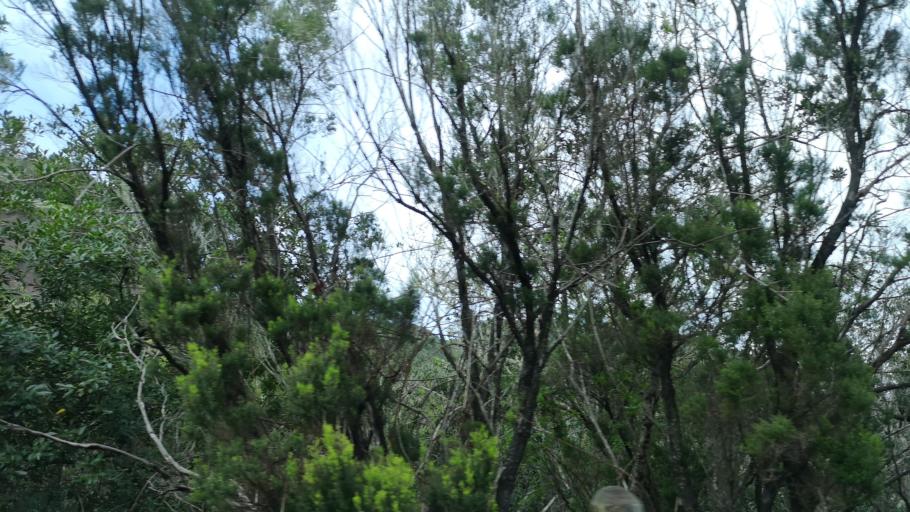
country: ES
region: Canary Islands
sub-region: Provincia de Santa Cruz de Tenerife
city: Vallehermosa
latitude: 28.1625
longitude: -17.2888
